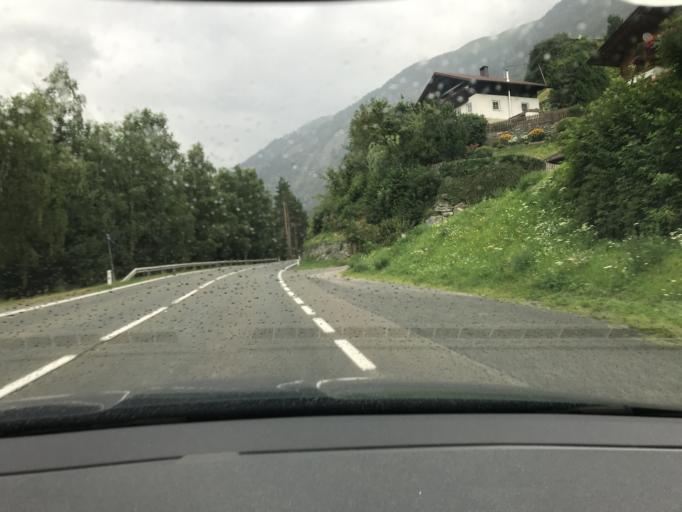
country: AT
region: Tyrol
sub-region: Politischer Bezirk Lienz
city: Matrei in Osttirol
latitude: 47.0057
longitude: 12.5410
